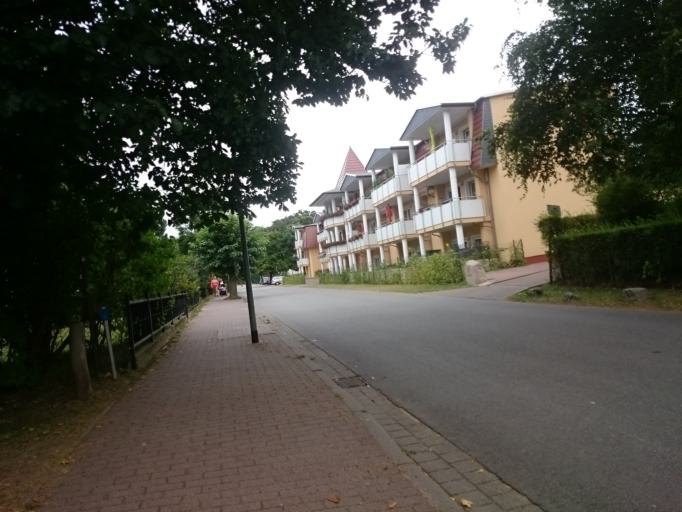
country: DE
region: Mecklenburg-Vorpommern
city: Koserow
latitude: 54.0540
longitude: 14.0024
